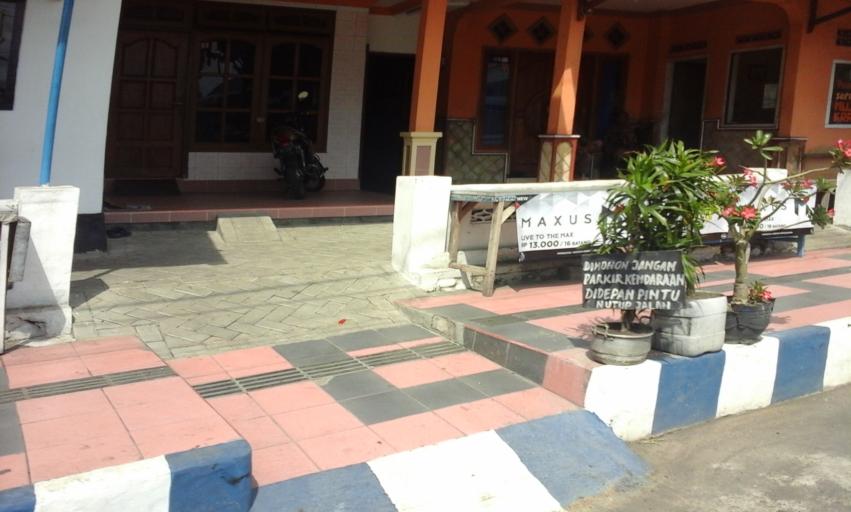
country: ID
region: East Java
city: Klatakan
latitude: -8.1431
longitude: 114.3995
